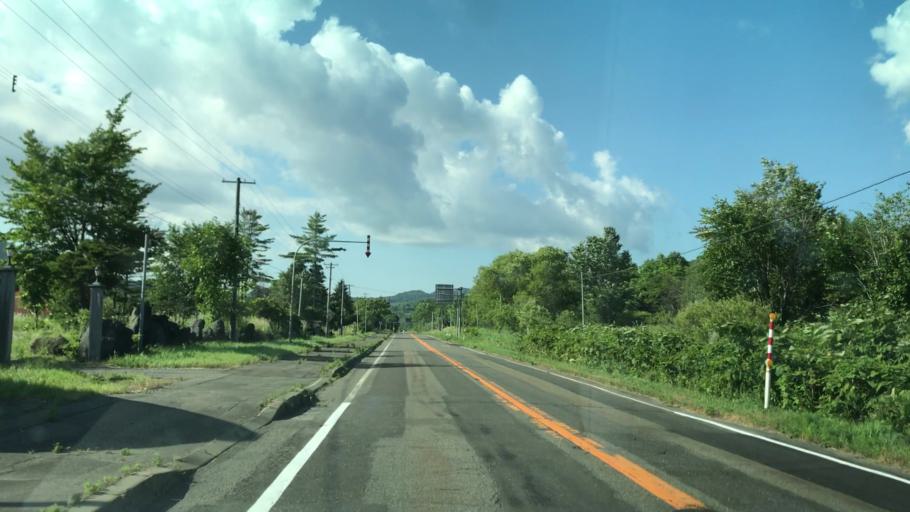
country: JP
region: Hokkaido
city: Shimo-furano
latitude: 42.8849
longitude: 142.4323
